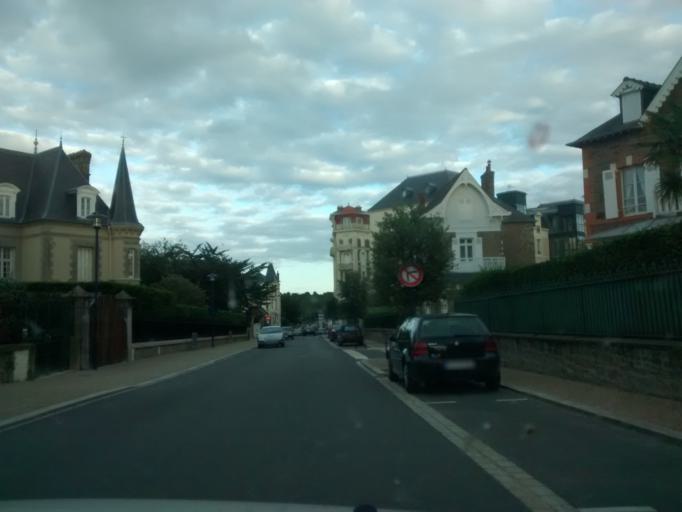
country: FR
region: Brittany
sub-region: Departement d'Ille-et-Vilaine
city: Saint-Lunaire
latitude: 48.6373
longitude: -2.1129
